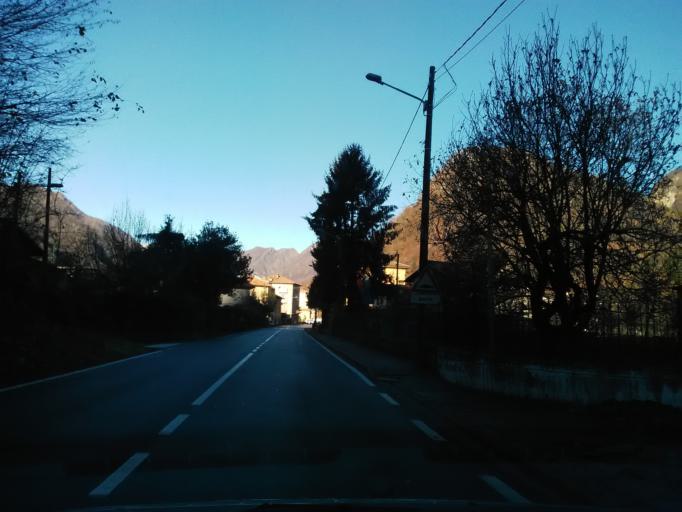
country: IT
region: Piedmont
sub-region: Provincia di Vercelli
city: Civiasco
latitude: 45.7909
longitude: 8.2784
